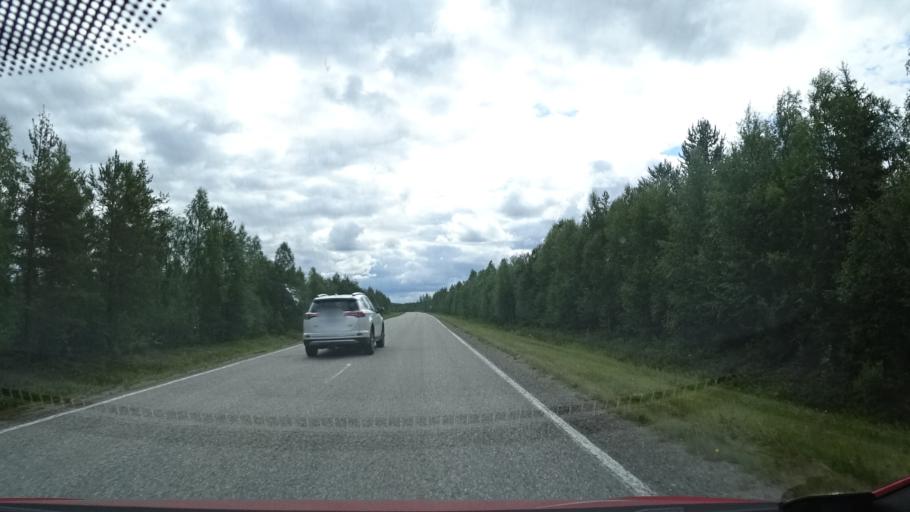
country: FI
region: Lapland
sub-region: Tunturi-Lappi
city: Kittilae
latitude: 67.4588
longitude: 24.9474
